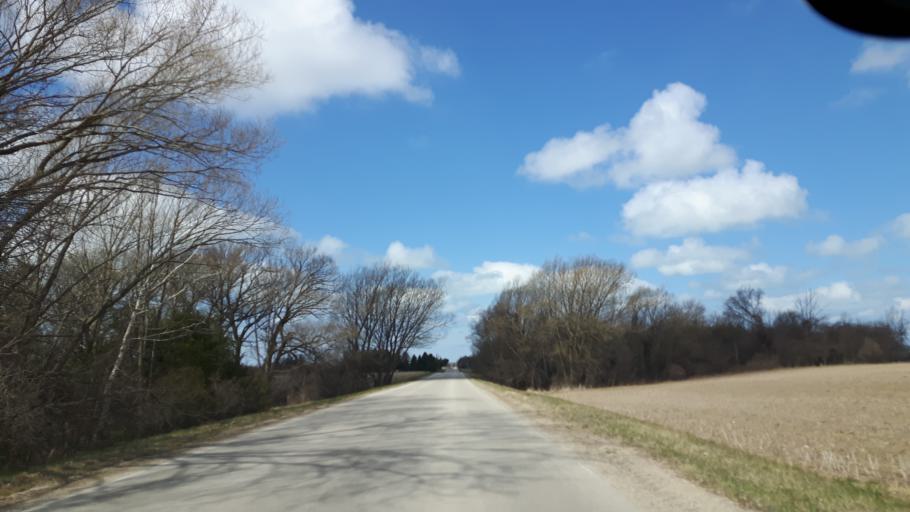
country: CA
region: Ontario
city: Goderich
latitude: 43.6984
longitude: -81.6970
